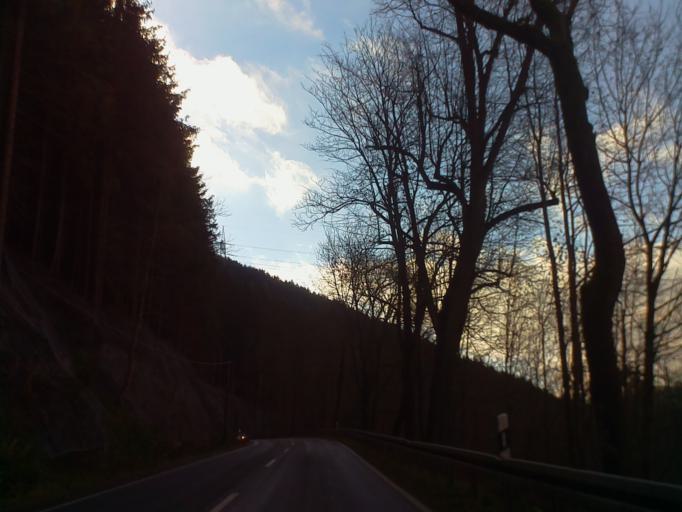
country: DE
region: Thuringia
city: Meuselbach
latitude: 50.5807
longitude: 11.0794
